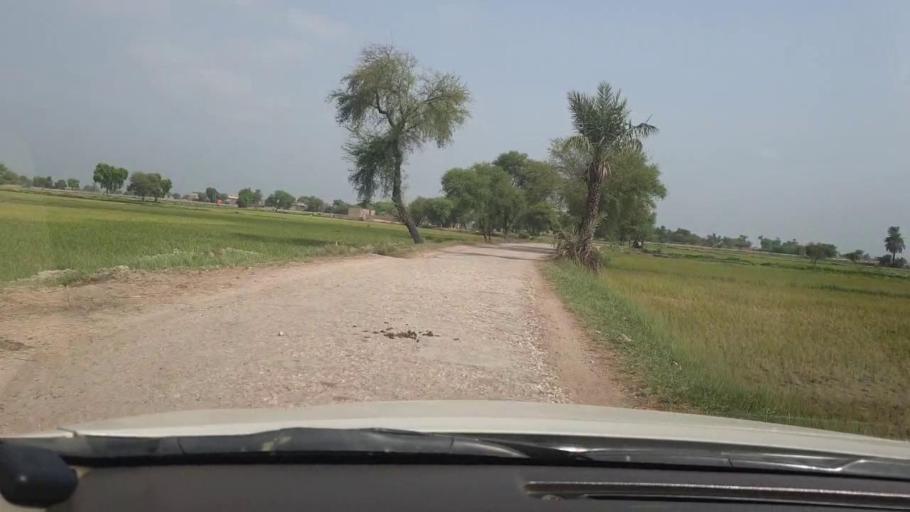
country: PK
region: Sindh
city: Shikarpur
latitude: 28.0015
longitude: 68.5940
